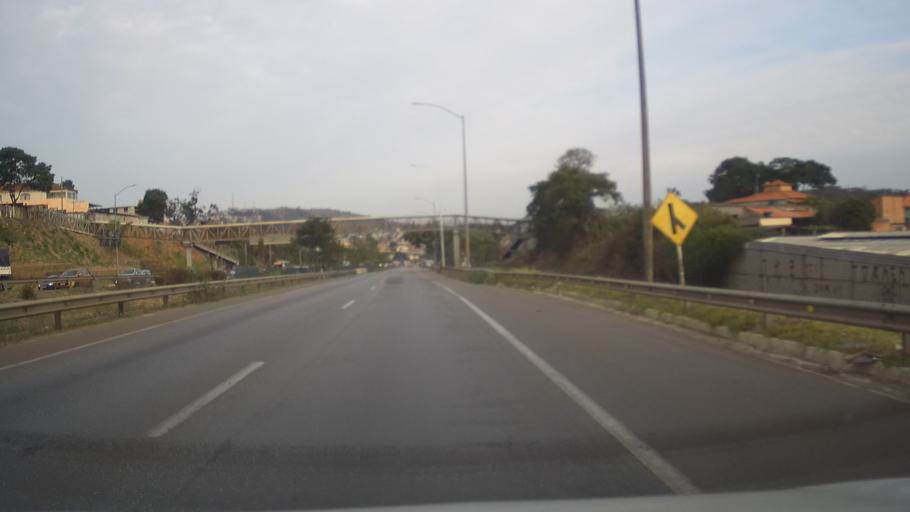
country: BR
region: Minas Gerais
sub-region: Belo Horizonte
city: Belo Horizonte
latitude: -19.8151
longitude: -43.9486
